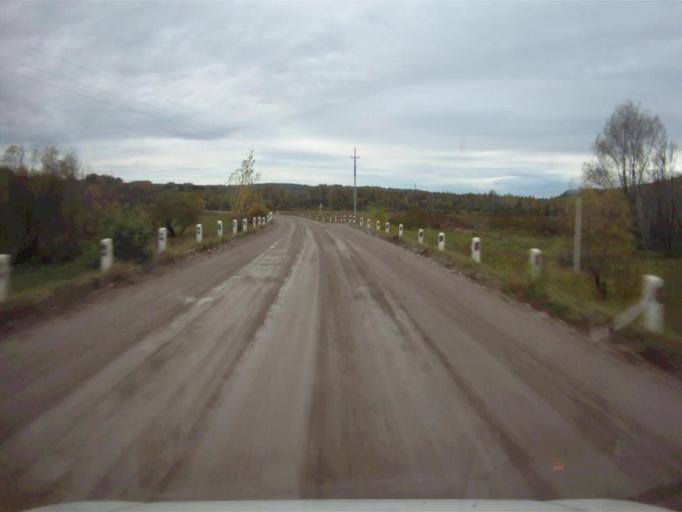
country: RU
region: Chelyabinsk
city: Nyazepetrovsk
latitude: 56.1247
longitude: 59.3544
